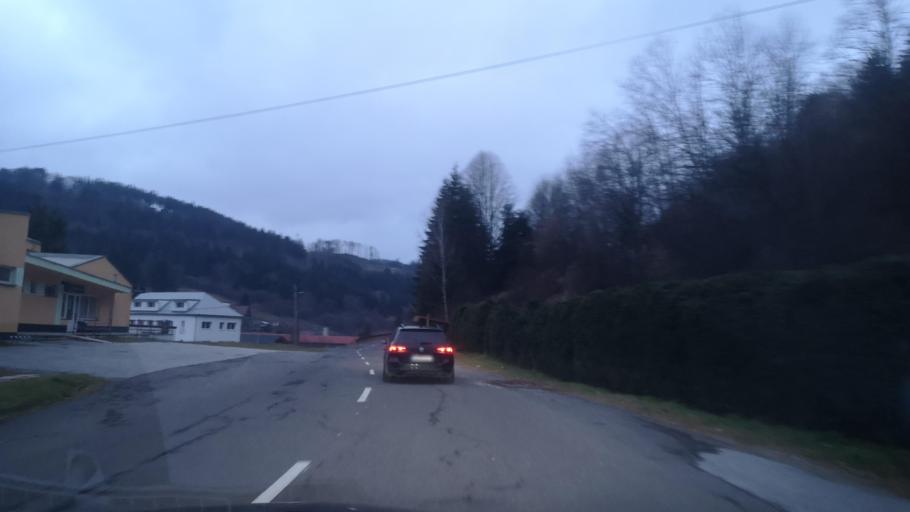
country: SK
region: Banskobystricky
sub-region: Okres Ziar nad Hronom
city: Kremnica
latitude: 48.7582
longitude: 18.9228
